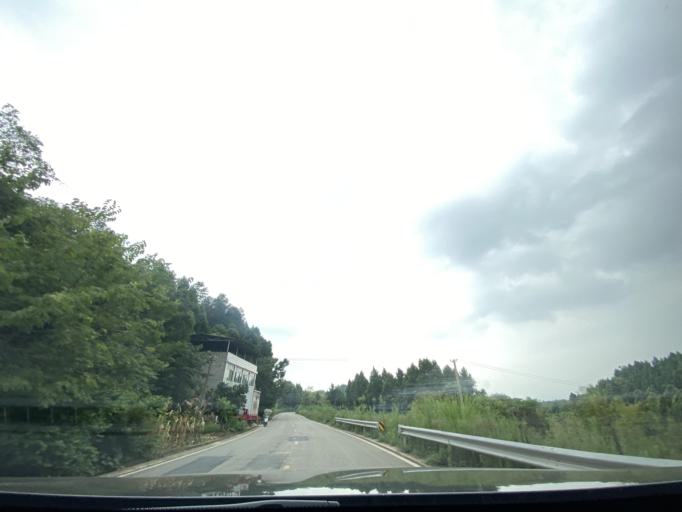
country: CN
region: Sichuan
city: Jiancheng
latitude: 30.5350
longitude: 104.5343
